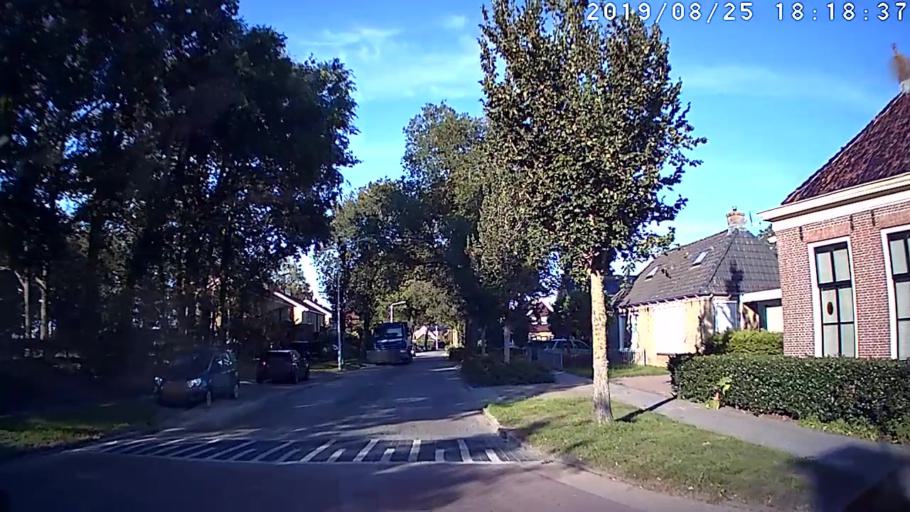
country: NL
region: Friesland
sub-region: Gemeente Gaasterlan-Sleat
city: Balk
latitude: 52.8719
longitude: 5.5996
